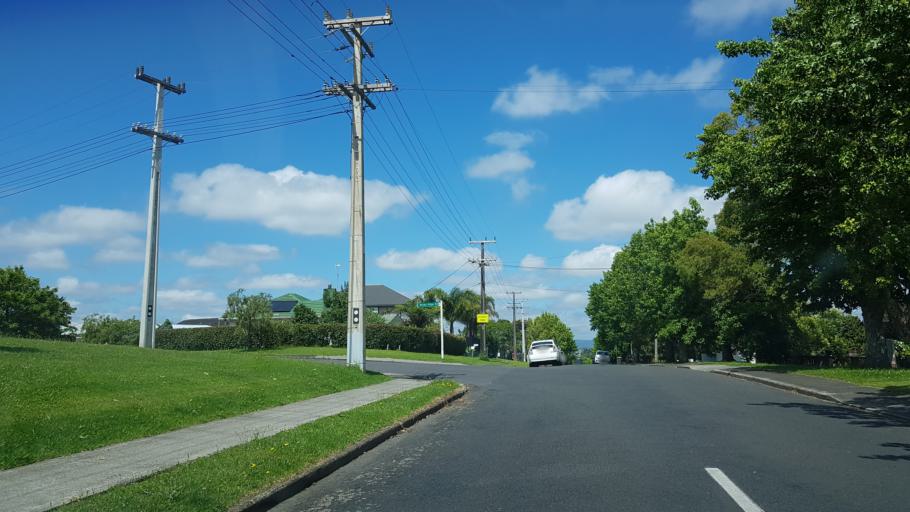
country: NZ
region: Auckland
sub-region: Auckland
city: North Shore
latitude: -36.7900
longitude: 174.7134
